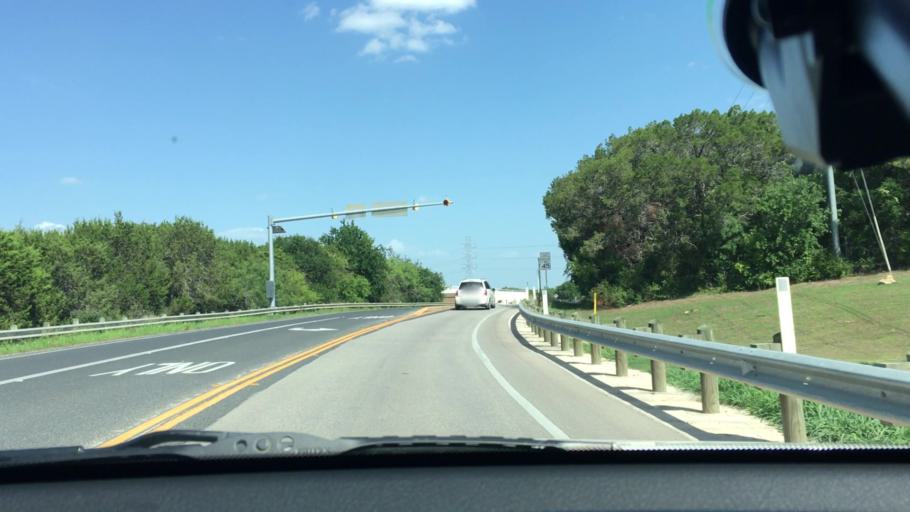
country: US
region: Texas
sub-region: Comal County
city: Garden Ridge
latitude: 29.6105
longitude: -98.3351
